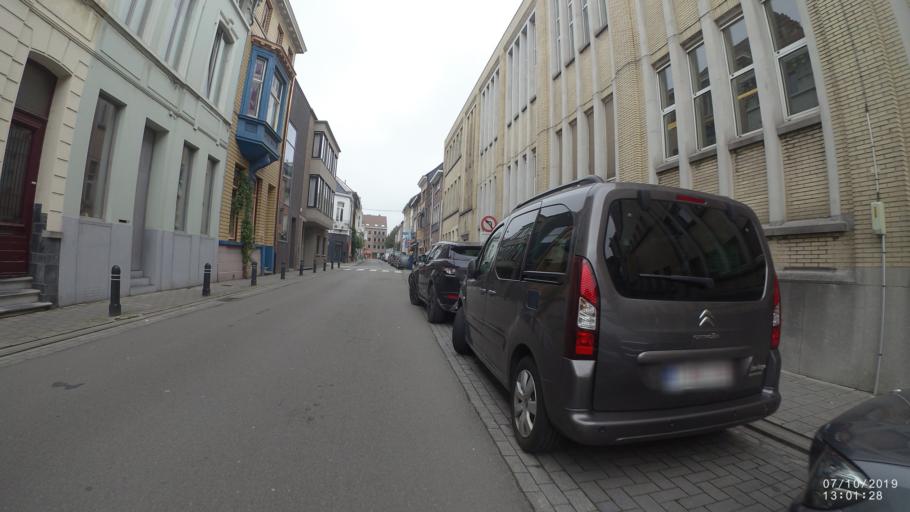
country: BE
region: Flanders
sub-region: Provincie Oost-Vlaanderen
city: Ledeberg
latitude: 51.0595
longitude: 3.7490
